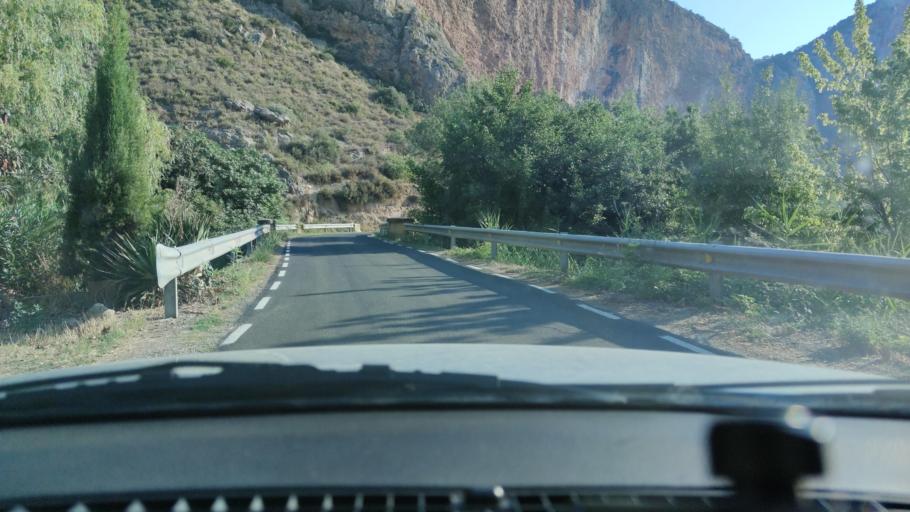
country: ES
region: Catalonia
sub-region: Provincia de Lleida
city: Camarasa
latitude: 41.8723
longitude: 0.8434
